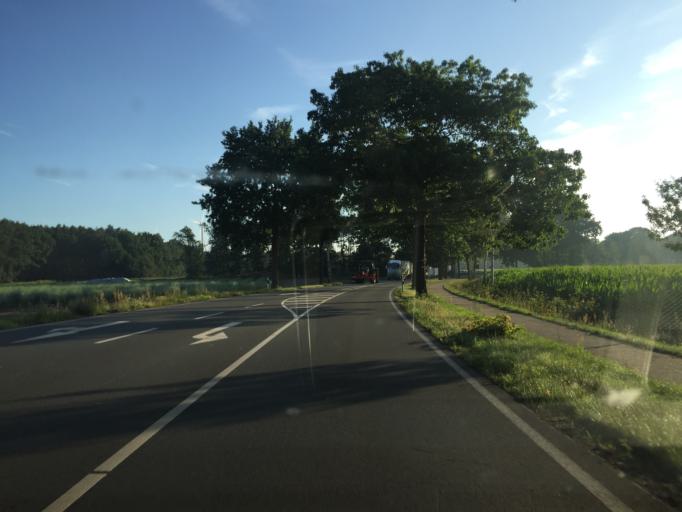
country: DE
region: Lower Saxony
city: Hauslingen
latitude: 52.7987
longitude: 9.4166
